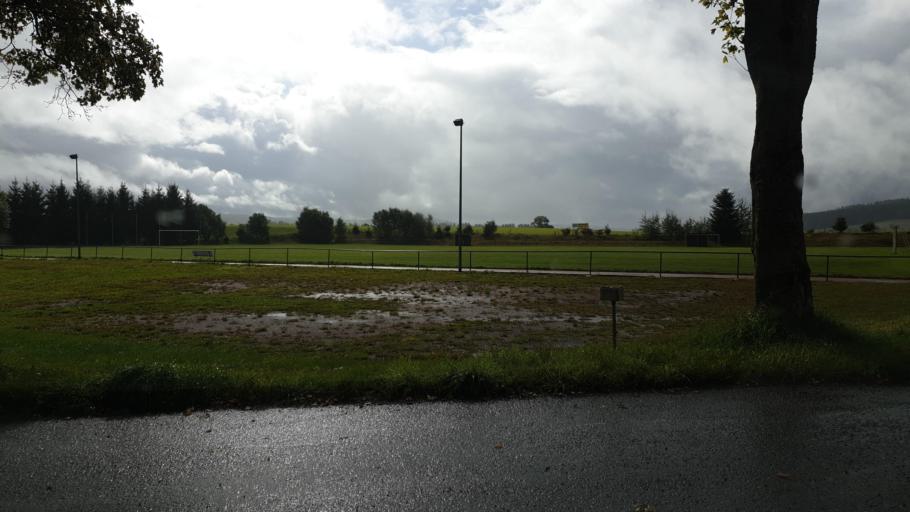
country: DE
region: Saxony
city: Rechenberg-Bienenmuhle
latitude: 50.7105
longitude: 13.4986
